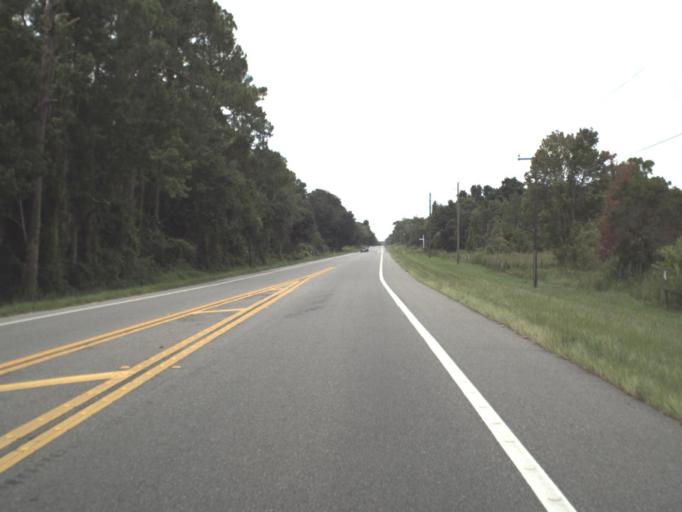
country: US
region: Florida
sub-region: Hernando County
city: Ridge Manor
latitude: 28.5282
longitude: -82.1654
